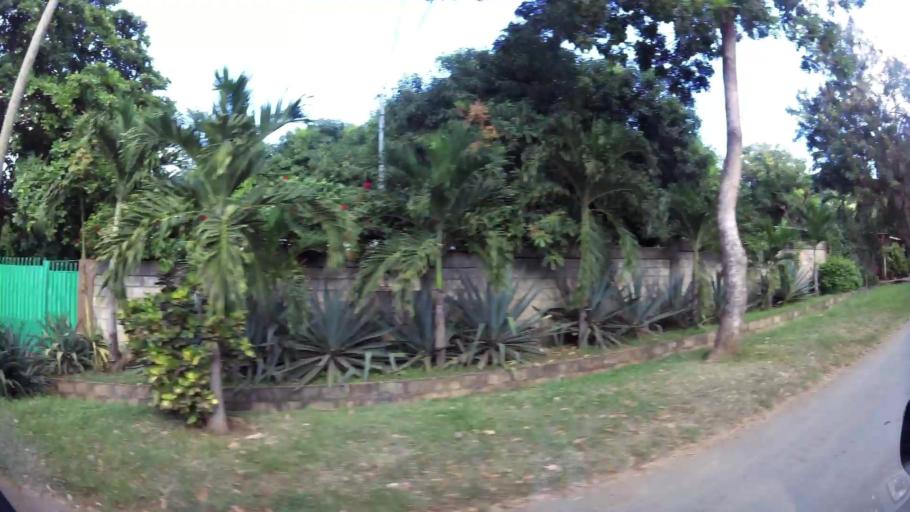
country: CR
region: Guanacaste
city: Sardinal
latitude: 10.5580
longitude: -85.6902
